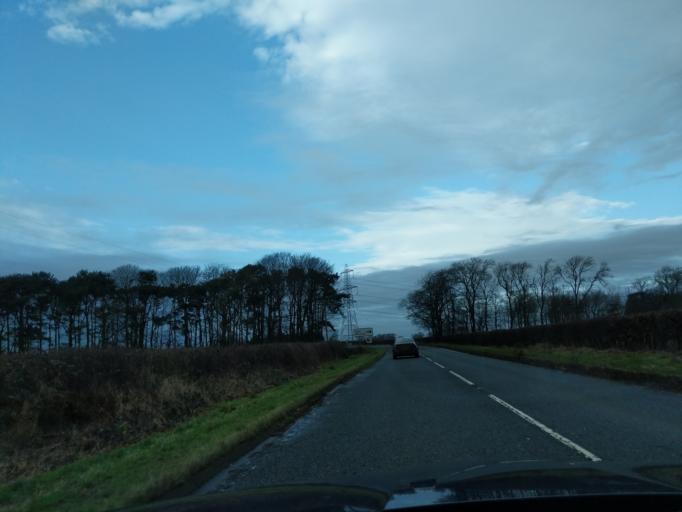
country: GB
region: England
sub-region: Northumberland
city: Meldon
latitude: 55.1003
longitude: -1.8253
